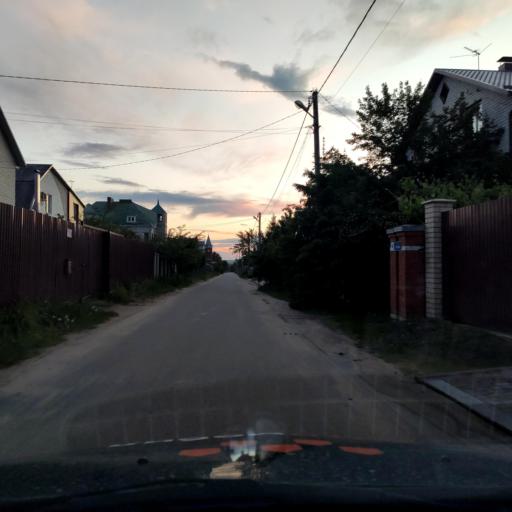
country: RU
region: Voronezj
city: Podgornoye
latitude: 51.7464
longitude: 39.1606
